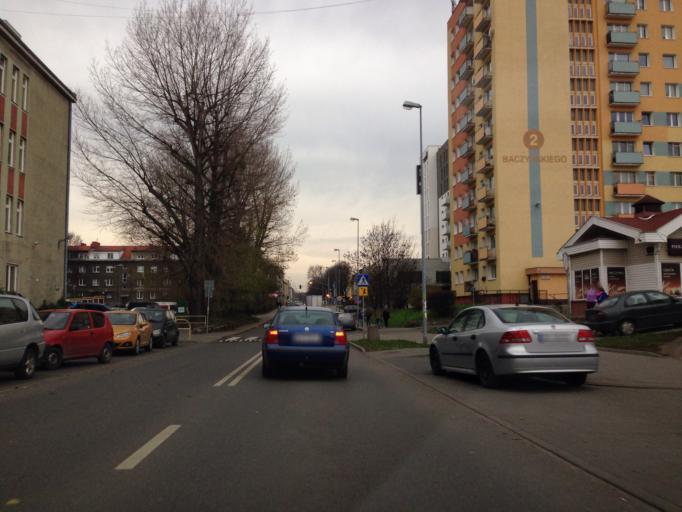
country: PL
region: Pomeranian Voivodeship
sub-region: Gdansk
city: Gdansk
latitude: 54.3877
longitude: 18.6255
